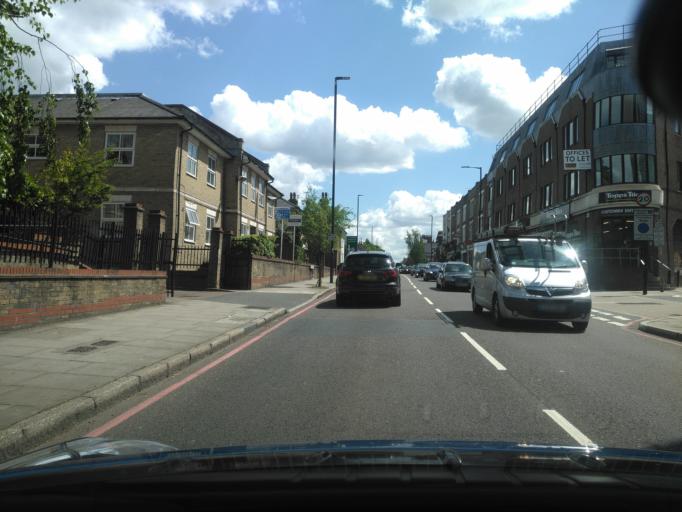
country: GB
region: England
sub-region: Greater London
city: Crouch End
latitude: 51.5789
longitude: -0.1499
